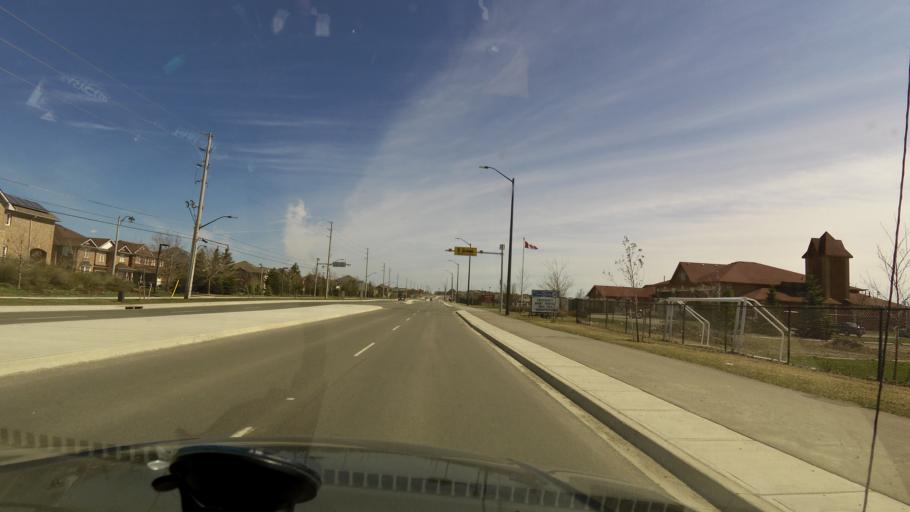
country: CA
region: Ontario
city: Brampton
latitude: 43.6876
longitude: -79.8339
